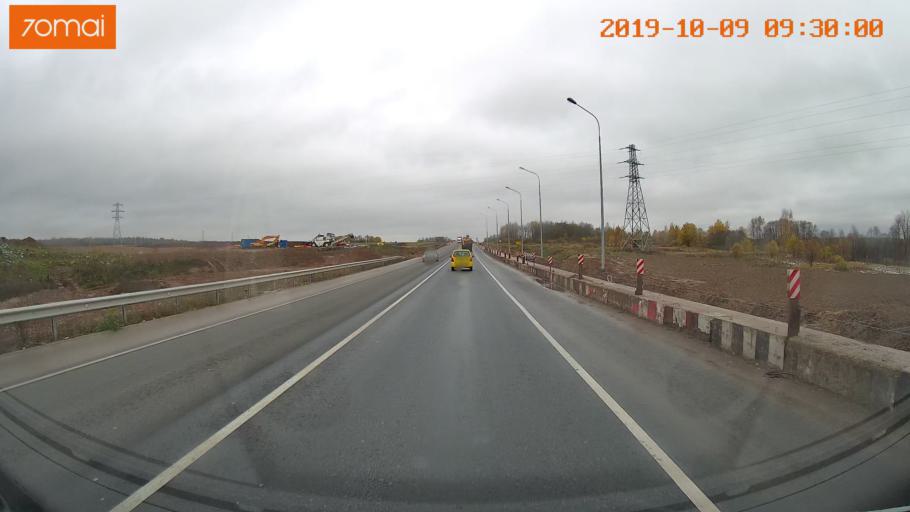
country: RU
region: Vologda
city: Vologda
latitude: 59.1364
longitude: 39.9530
